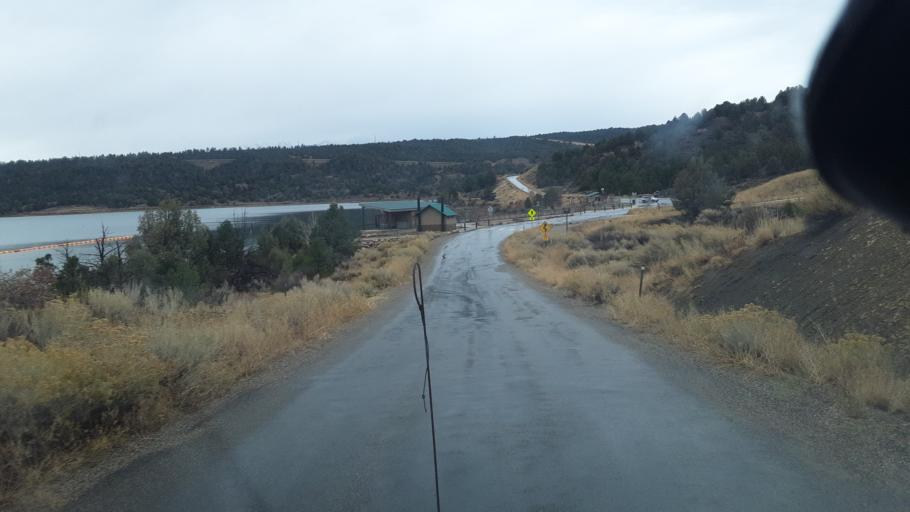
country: US
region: Colorado
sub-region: La Plata County
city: Durango
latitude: 37.2318
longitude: -107.9058
